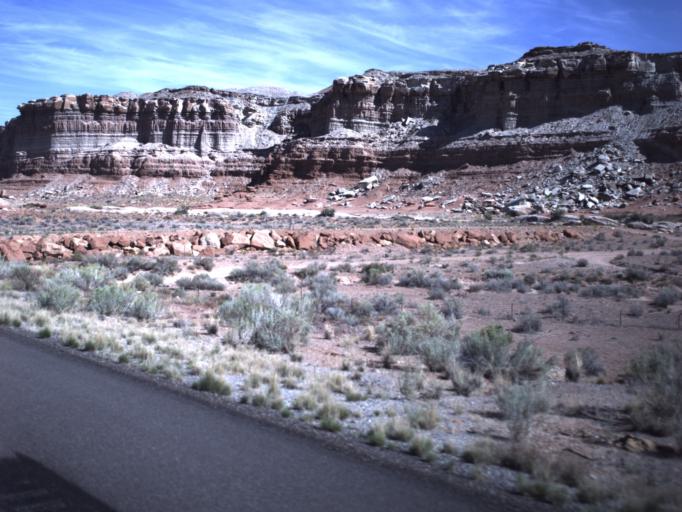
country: US
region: Utah
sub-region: Carbon County
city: East Carbon City
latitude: 38.9242
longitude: -110.4197
